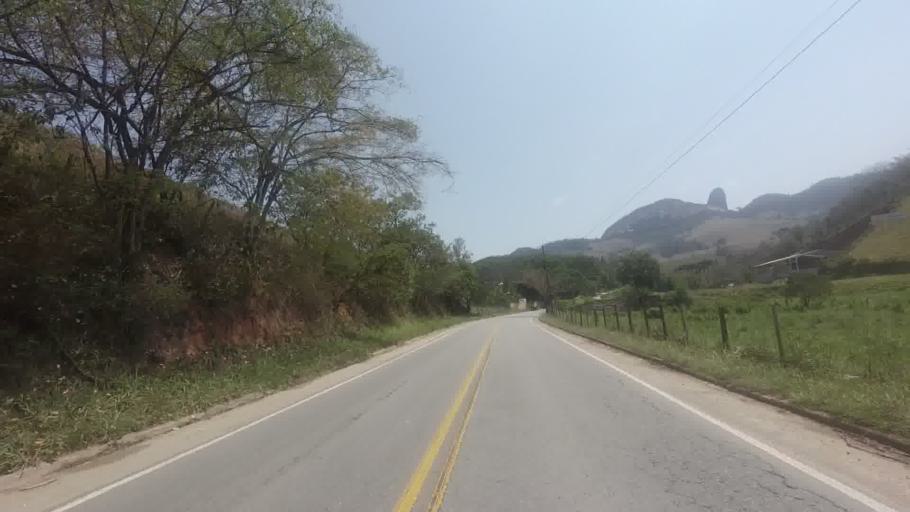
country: BR
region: Espirito Santo
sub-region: Cachoeiro De Itapemirim
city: Cachoeiro de Itapemirim
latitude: -20.8613
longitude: -41.0488
